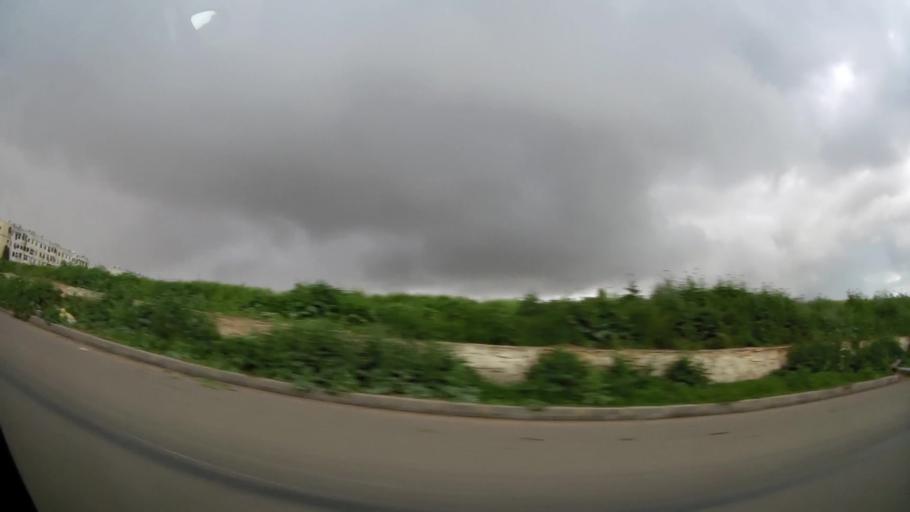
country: MA
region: Grand Casablanca
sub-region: Mediouna
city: Tit Mellil
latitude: 33.5689
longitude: -7.5143
